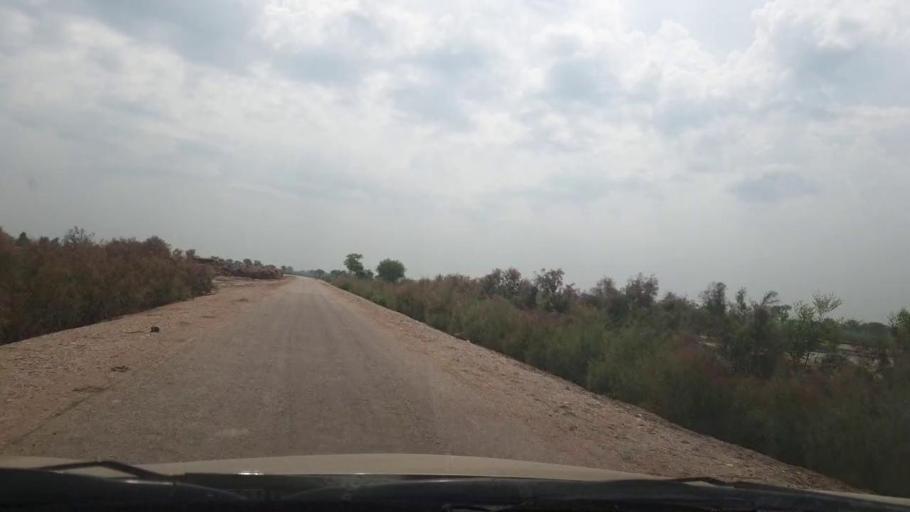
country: PK
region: Sindh
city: Ratodero
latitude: 27.6963
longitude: 68.2090
